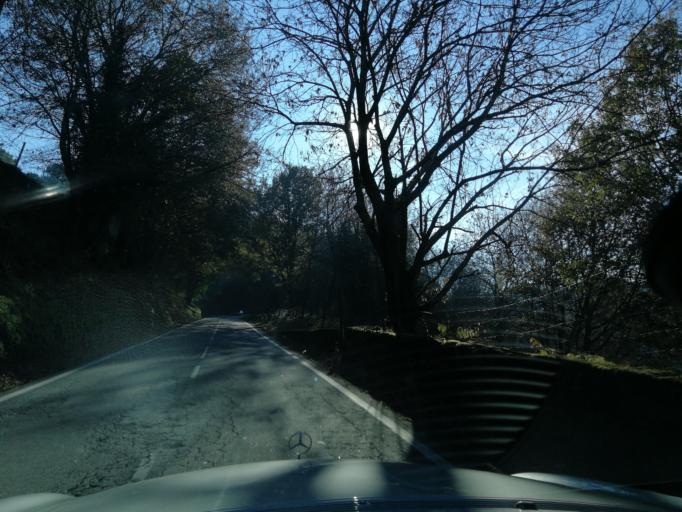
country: PT
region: Braga
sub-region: Braga
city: Adaufe
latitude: 41.5758
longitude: -8.3873
